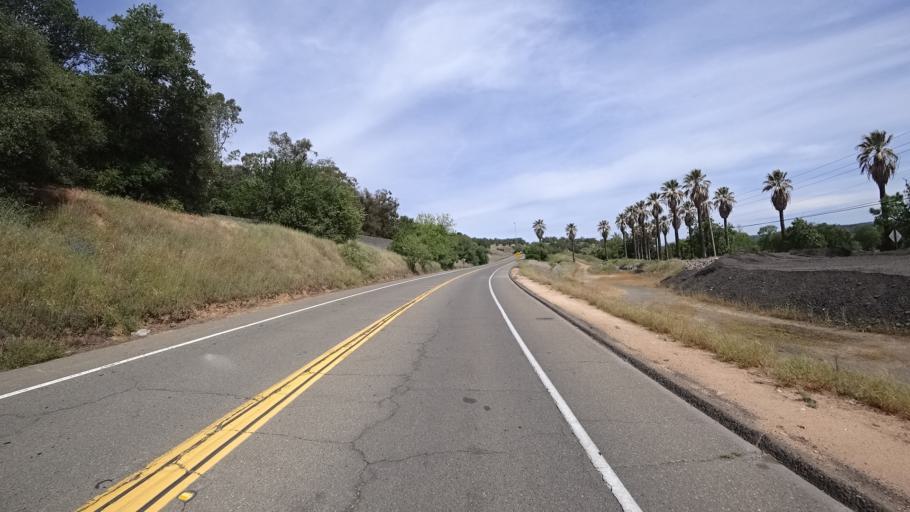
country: US
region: California
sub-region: Placer County
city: Loomis
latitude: 38.8360
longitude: -121.2202
